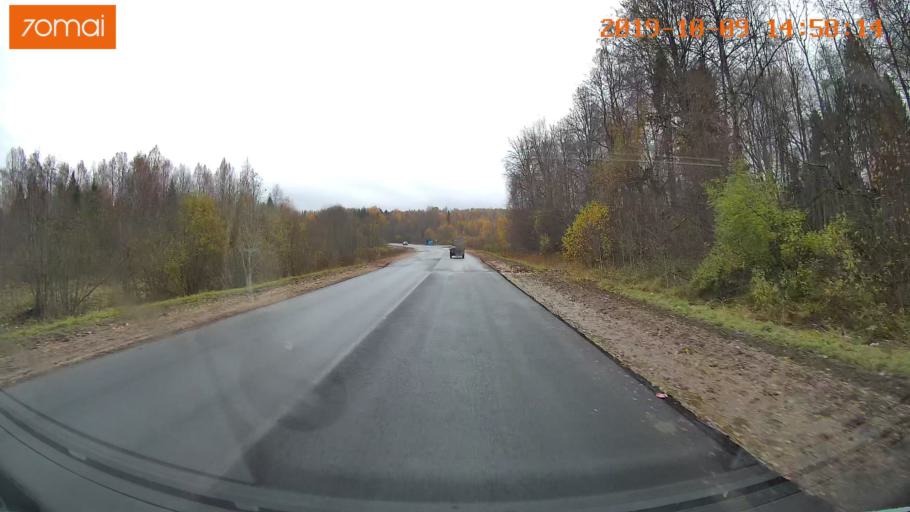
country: RU
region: Kostroma
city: Chistyye Bory
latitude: 58.3289
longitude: 41.6539
